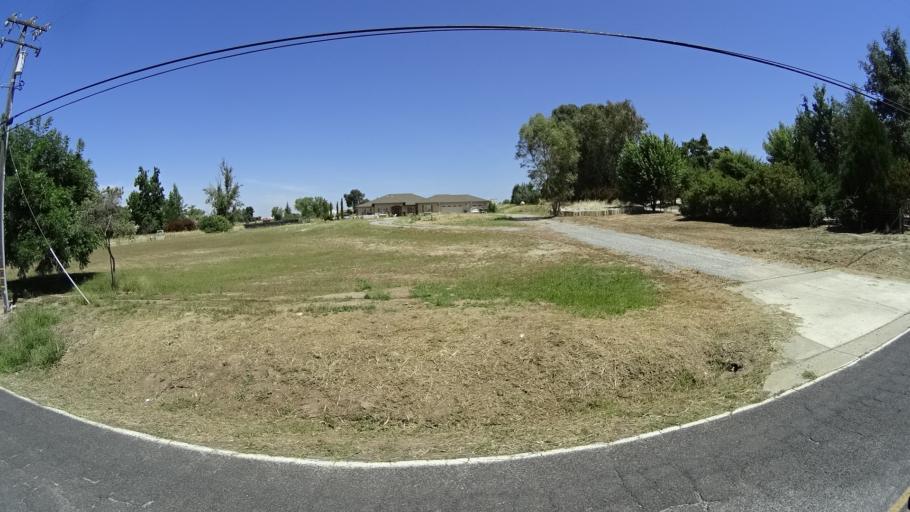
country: US
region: California
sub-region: Calaveras County
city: Rancho Calaveras
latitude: 38.1486
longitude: -120.9143
